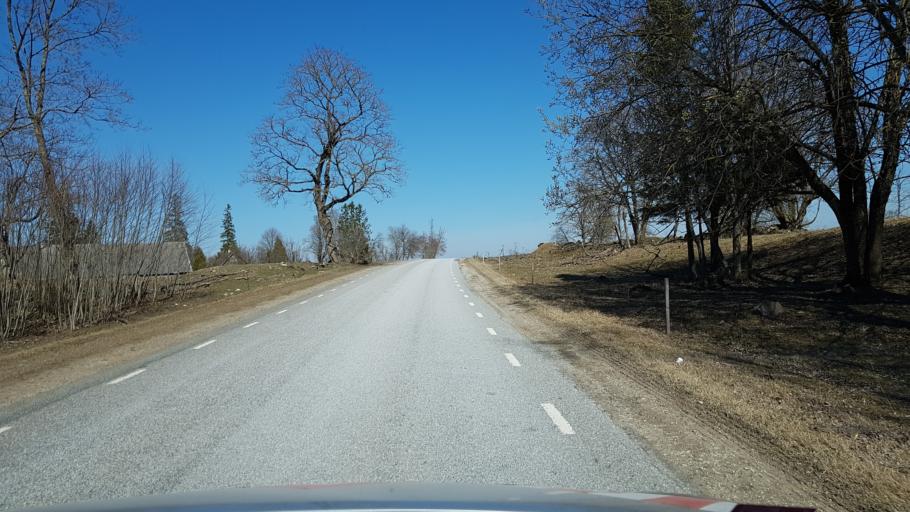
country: EE
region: Laeaene-Virumaa
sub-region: Tamsalu vald
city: Tamsalu
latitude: 59.0586
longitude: 26.1024
